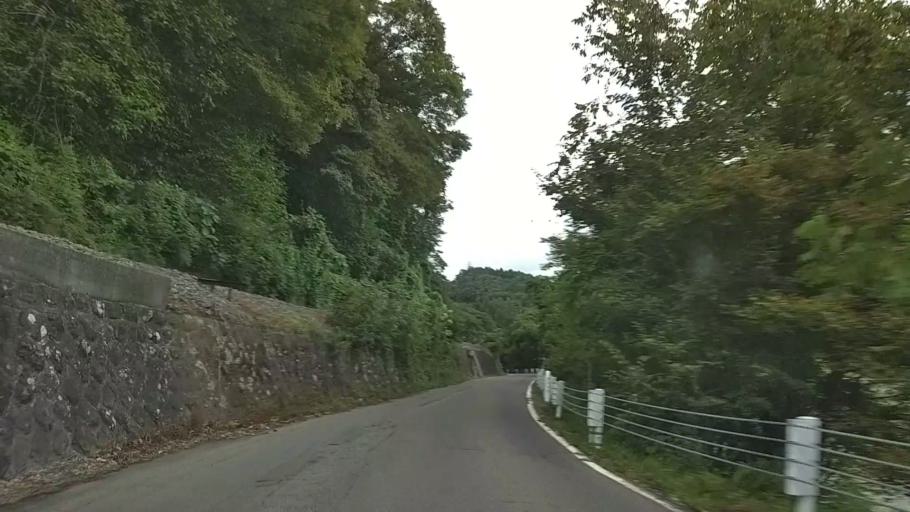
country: JP
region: Nagano
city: Iiyama
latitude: 36.8024
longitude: 138.3436
